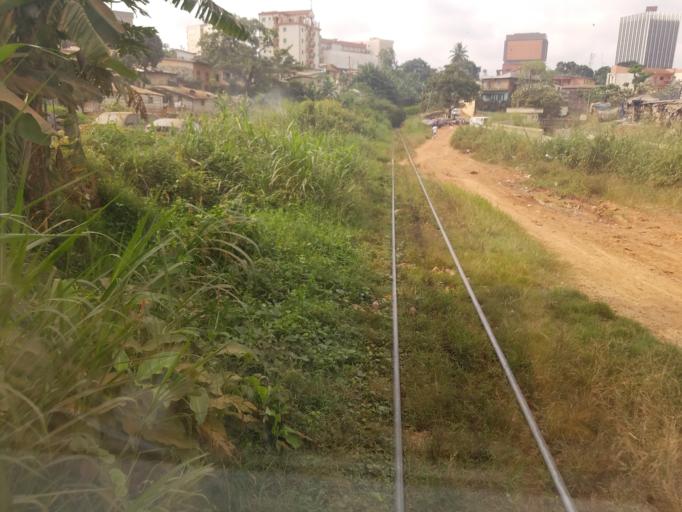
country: CM
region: Centre
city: Yaounde
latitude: 3.8645
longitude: 11.5245
